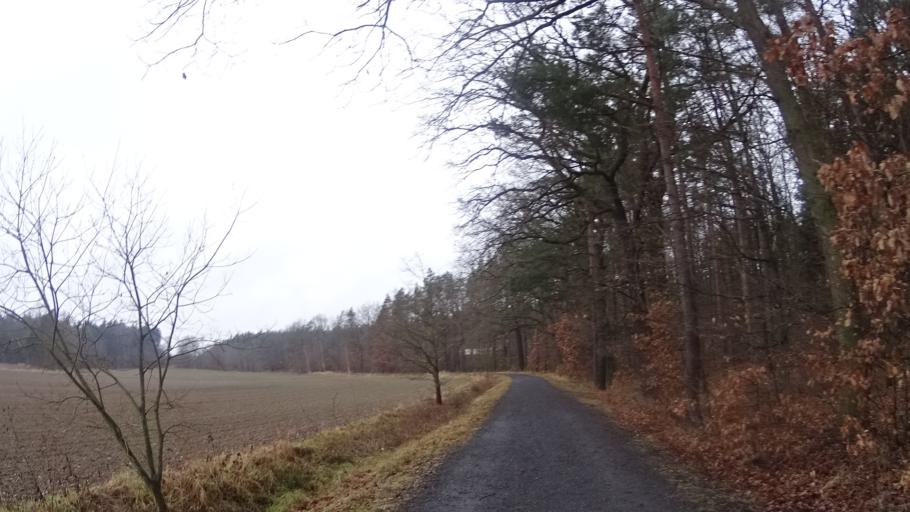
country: DE
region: Thuringia
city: Tissa
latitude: 50.8632
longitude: 11.7529
